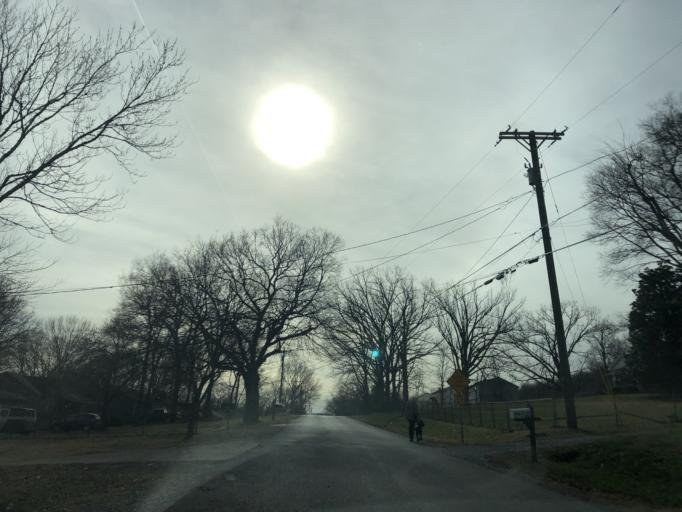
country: US
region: Tennessee
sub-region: Davidson County
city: Nashville
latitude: 36.2222
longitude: -86.7378
